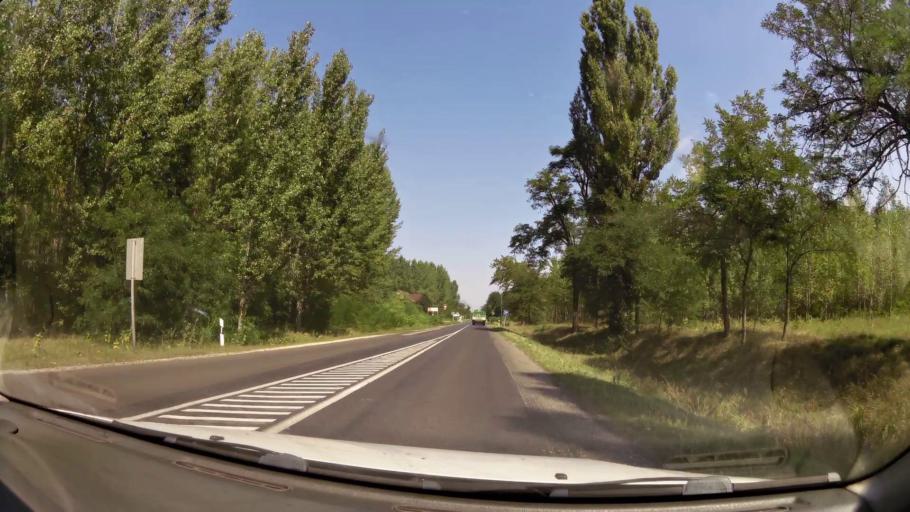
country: HU
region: Pest
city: Tapioszolos
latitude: 47.2892
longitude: 19.8673
